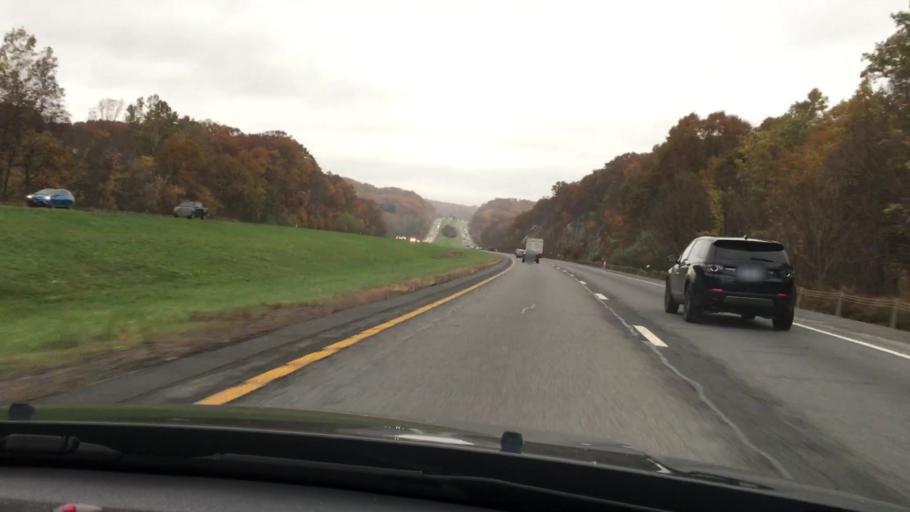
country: US
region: New York
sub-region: Putnam County
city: Brewster Hill
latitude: 41.4419
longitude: -73.6326
